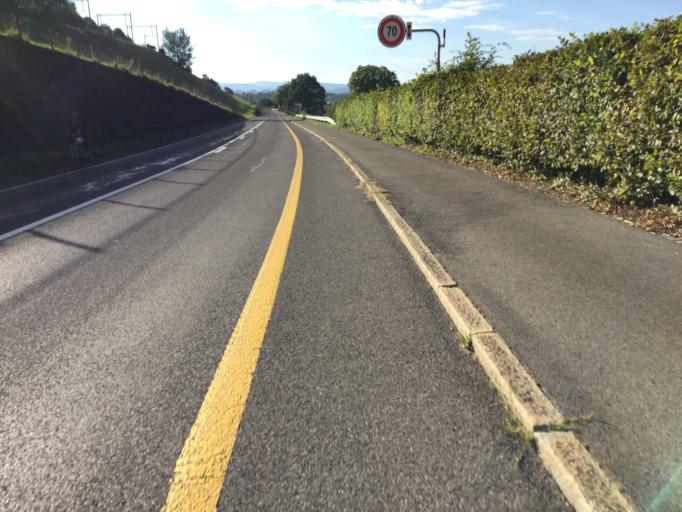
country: CH
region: Bern
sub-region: Frutigen-Niedersimmental District
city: Wimmis
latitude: 46.7044
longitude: 7.6533
